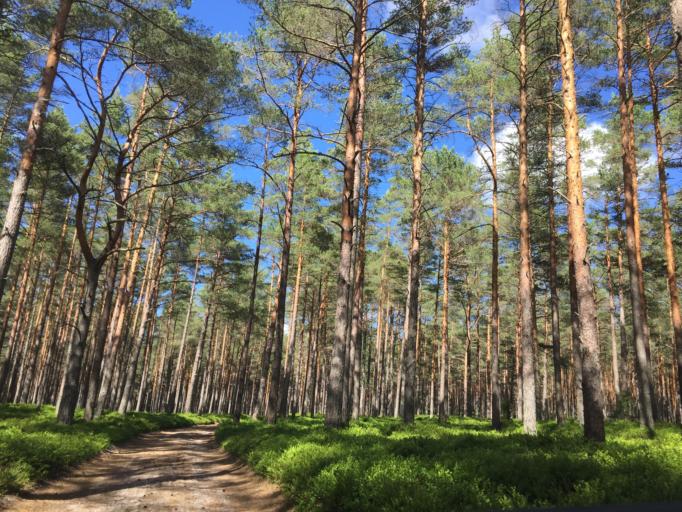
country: LV
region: Ventspils
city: Ventspils
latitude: 57.4661
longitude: 21.6379
